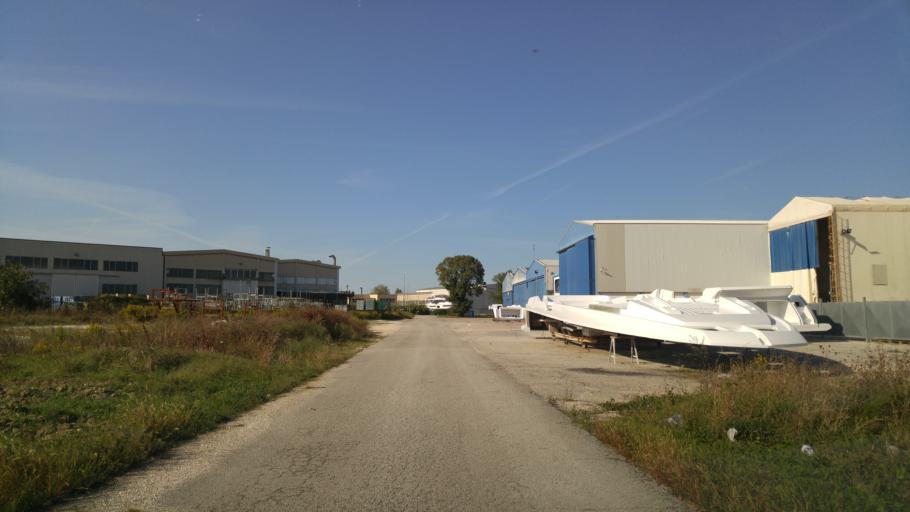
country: IT
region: The Marches
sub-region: Provincia di Pesaro e Urbino
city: Bellocchi
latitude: 43.7938
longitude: 13.0205
